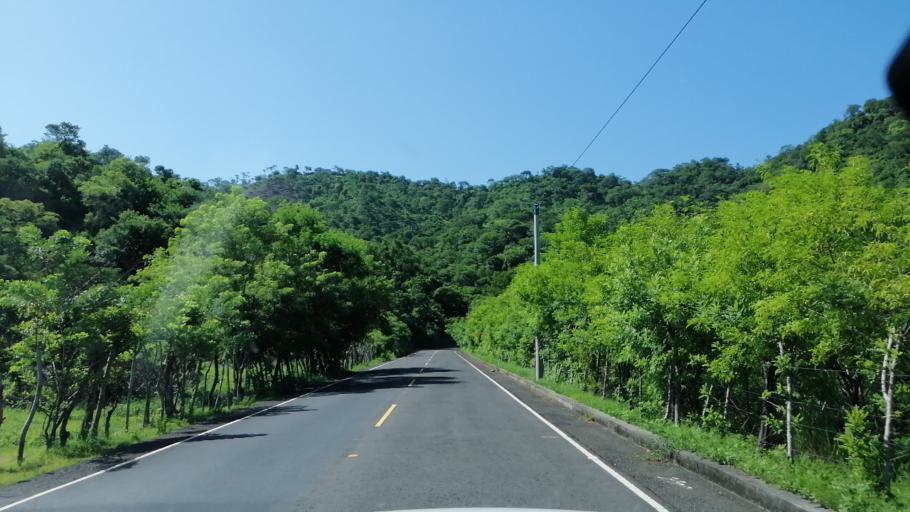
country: HN
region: Lempira
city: La Virtud
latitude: 13.9813
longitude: -88.7576
